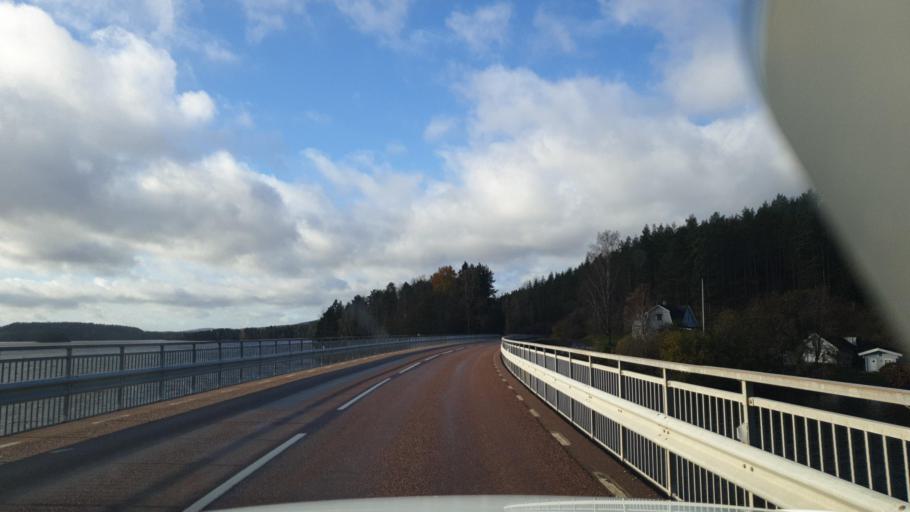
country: SE
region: Vaermland
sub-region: Grums Kommun
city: Slottsbron
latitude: 59.4568
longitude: 12.9312
